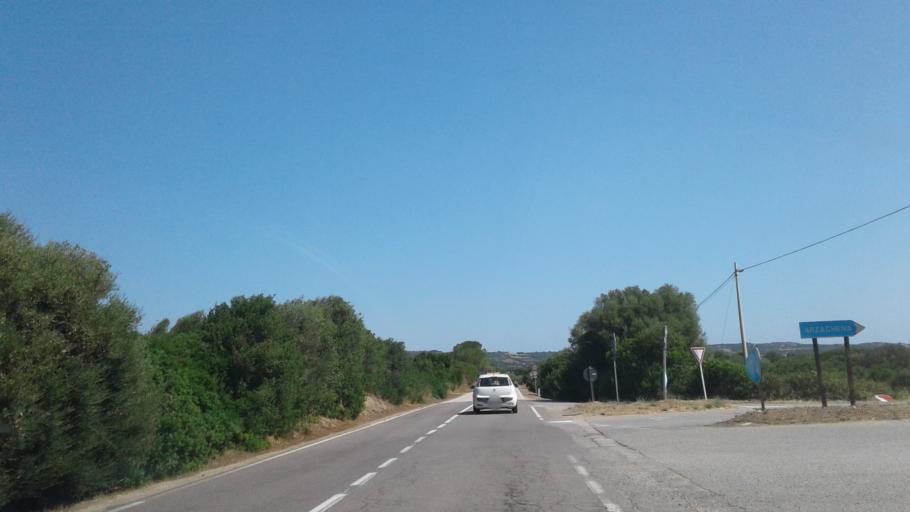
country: IT
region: Sardinia
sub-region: Provincia di Olbia-Tempio
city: Luogosanto
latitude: 41.1120
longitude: 9.2625
